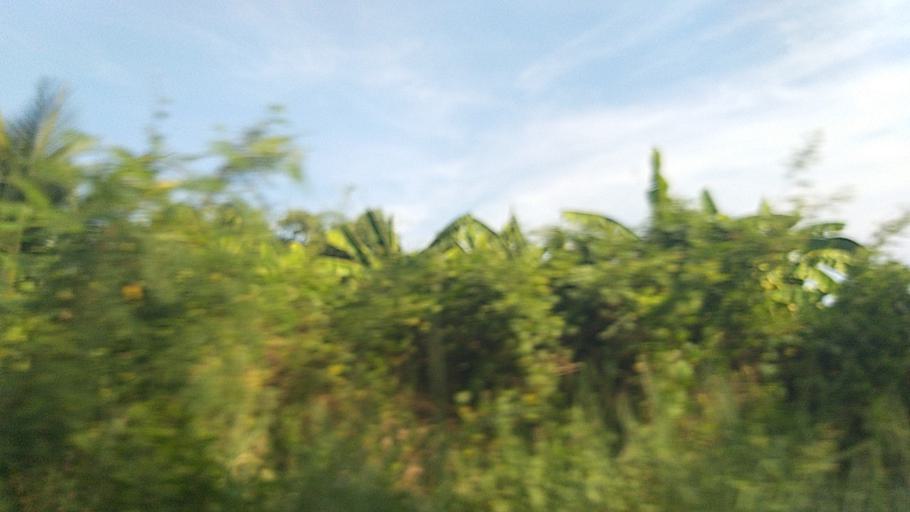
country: TH
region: Pathum Thani
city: Thanyaburi
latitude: 14.0082
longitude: 100.7315
